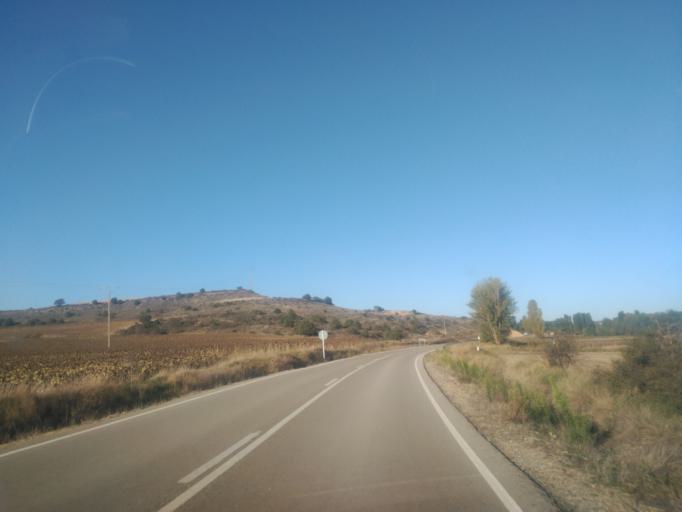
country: ES
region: Castille and Leon
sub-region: Provincia de Soria
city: Alcubilla de Avellaneda
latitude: 41.7549
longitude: -3.2552
